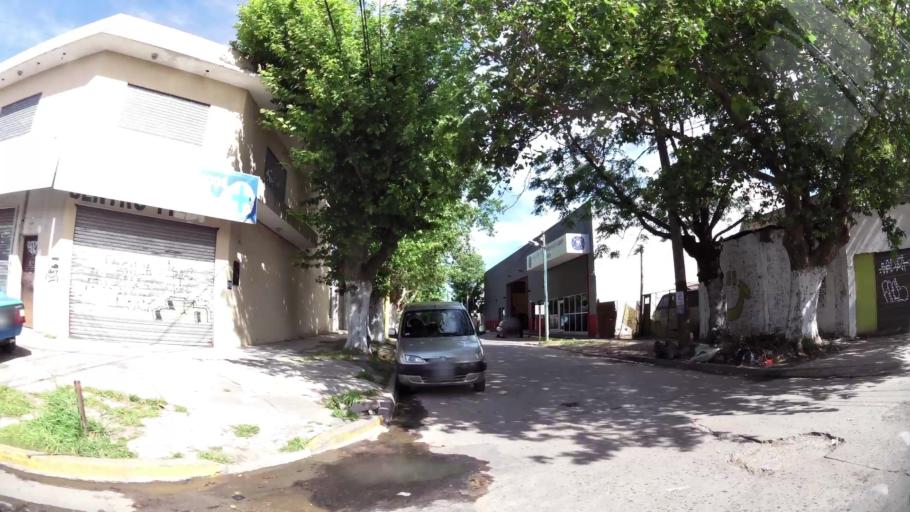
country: AR
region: Buenos Aires
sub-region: Partido de Quilmes
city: Quilmes
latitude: -34.7701
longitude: -58.2946
